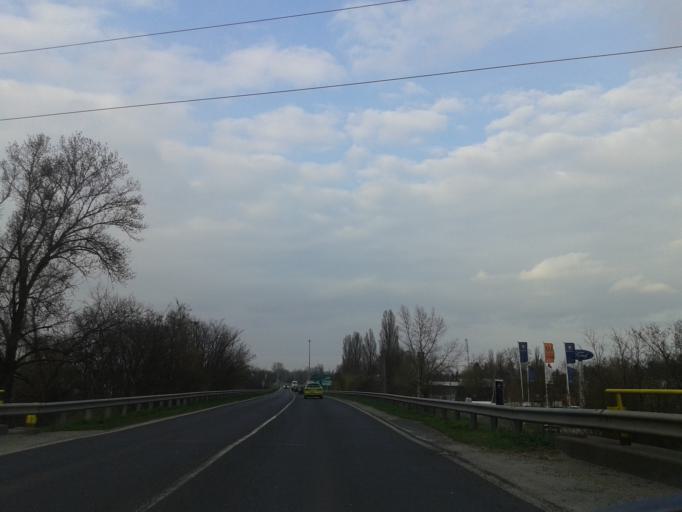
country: HU
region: Gyor-Moson-Sopron
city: Gyor
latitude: 47.7010
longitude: 17.6690
